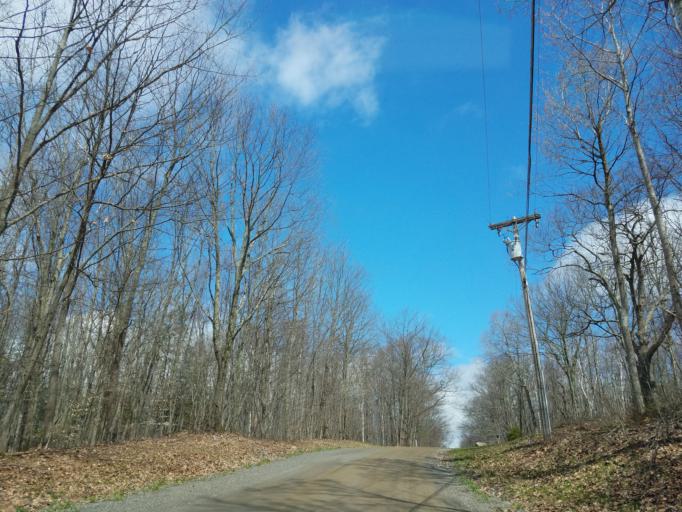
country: US
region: Connecticut
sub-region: Litchfield County
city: West Torrington
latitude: 41.7870
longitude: -73.1662
